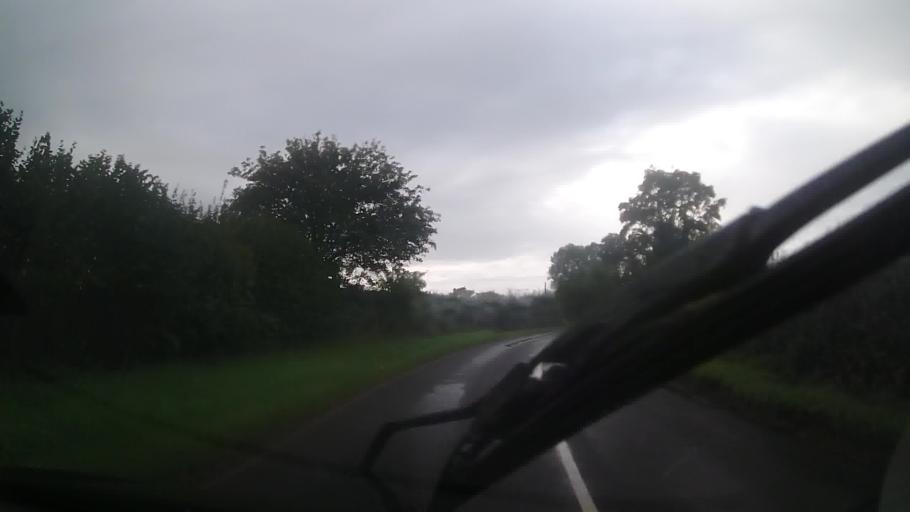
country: GB
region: England
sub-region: Oxfordshire
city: Stonesfield
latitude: 51.8727
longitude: -1.4008
